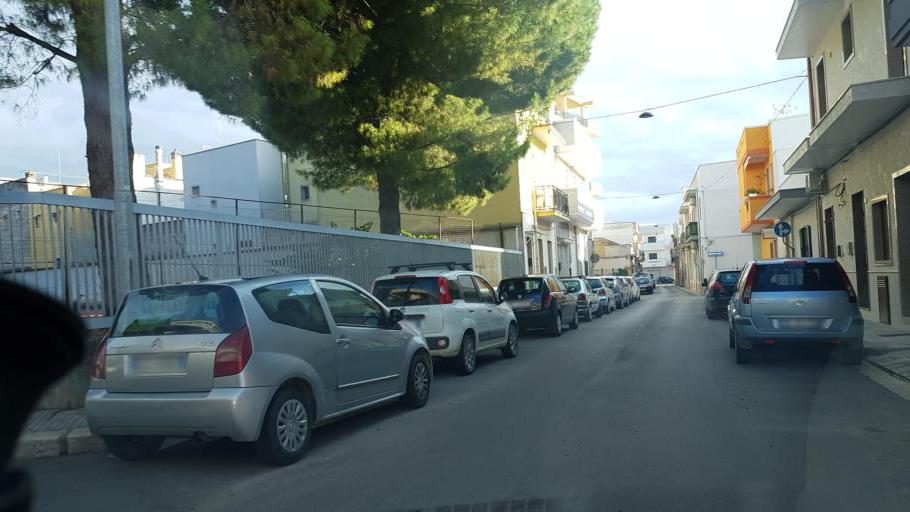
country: IT
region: Apulia
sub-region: Provincia di Brindisi
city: Francavilla Fontana
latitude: 40.5273
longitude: 17.5899
